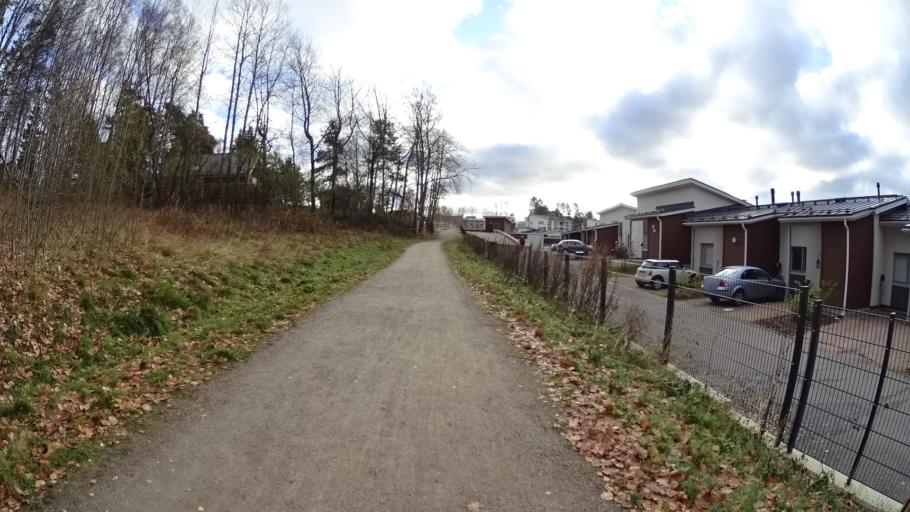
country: FI
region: Uusimaa
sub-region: Helsinki
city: Teekkarikylae
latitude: 60.2594
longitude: 24.8659
